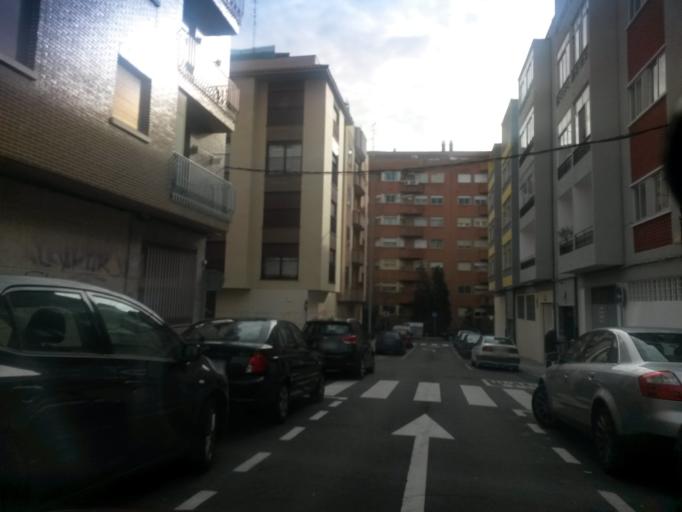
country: ES
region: Castille and Leon
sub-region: Provincia de Salamanca
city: Salamanca
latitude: 40.9757
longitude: -5.6568
